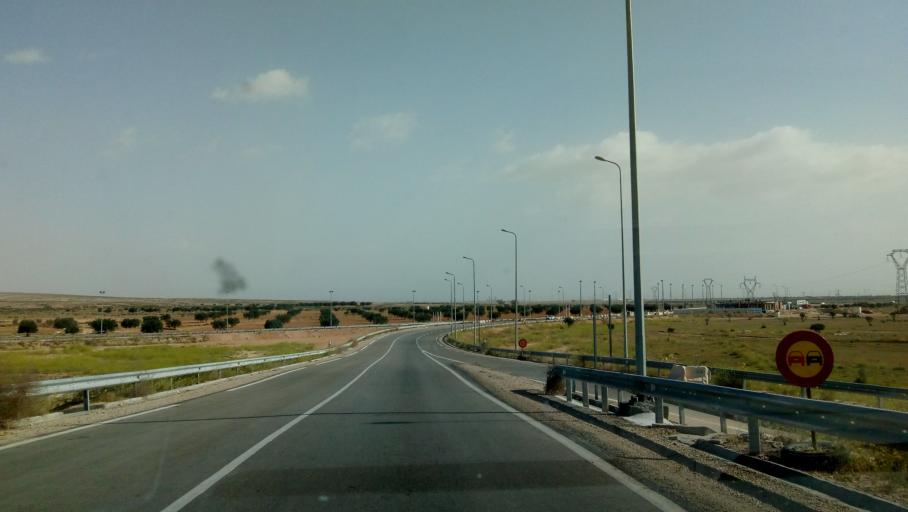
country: TN
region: Qabis
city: Gabes
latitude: 33.8819
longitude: 9.9967
